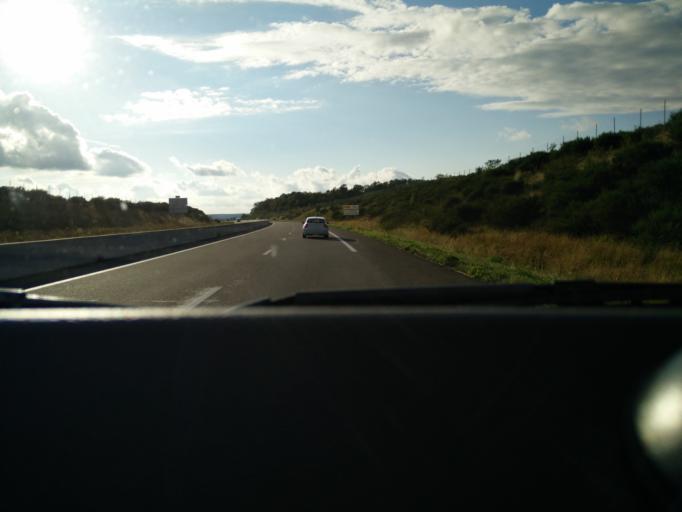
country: FR
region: Lorraine
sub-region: Departement de Meurthe-et-Moselle
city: Gerbeviller
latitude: 48.5268
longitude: 6.6323
